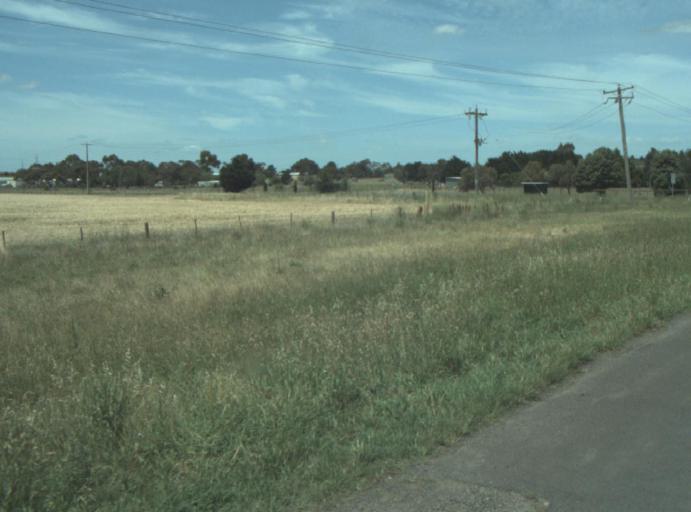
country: AU
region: Victoria
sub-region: Greater Geelong
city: Lara
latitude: -38.0171
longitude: 144.3519
